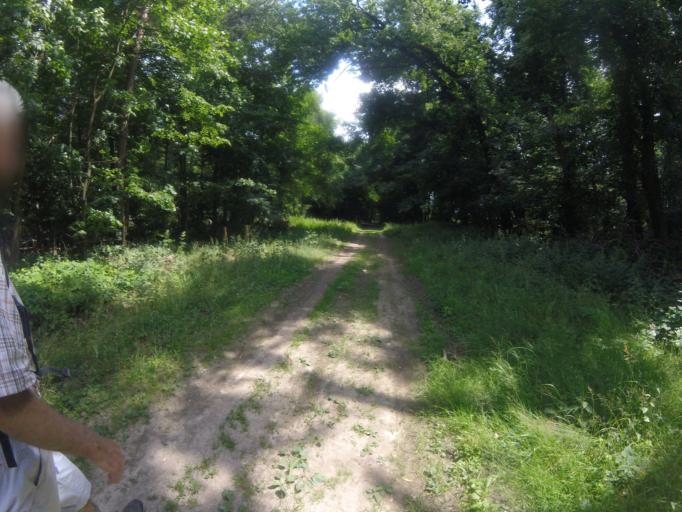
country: HU
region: Fejer
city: Szarliget
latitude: 47.5016
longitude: 18.4359
